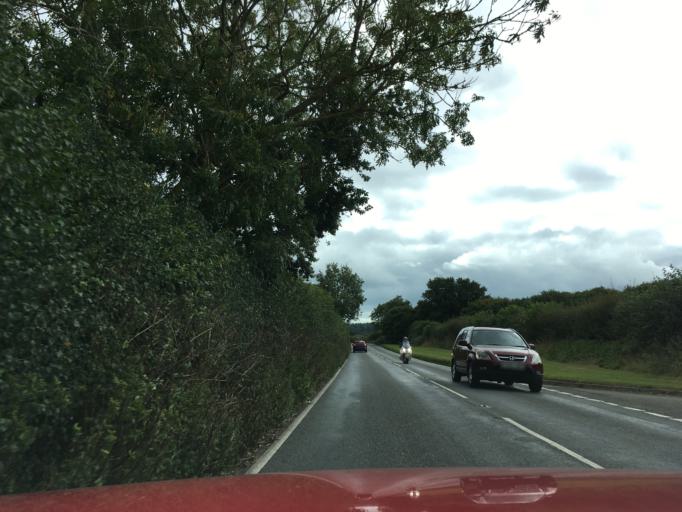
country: GB
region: England
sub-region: Devon
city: Exminster
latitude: 50.6500
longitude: -3.4820
